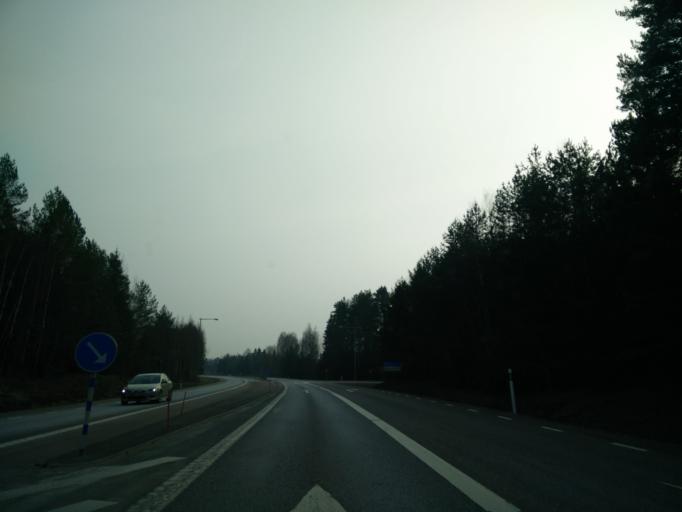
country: SE
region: Vaermland
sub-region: Forshaga Kommun
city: Forshaga
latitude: 59.4833
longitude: 13.4131
